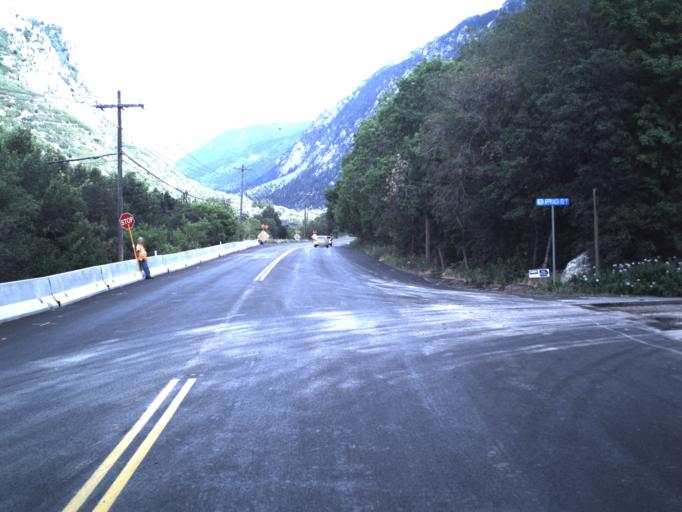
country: US
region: Utah
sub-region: Salt Lake County
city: Granite
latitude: 40.5730
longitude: -111.7833
